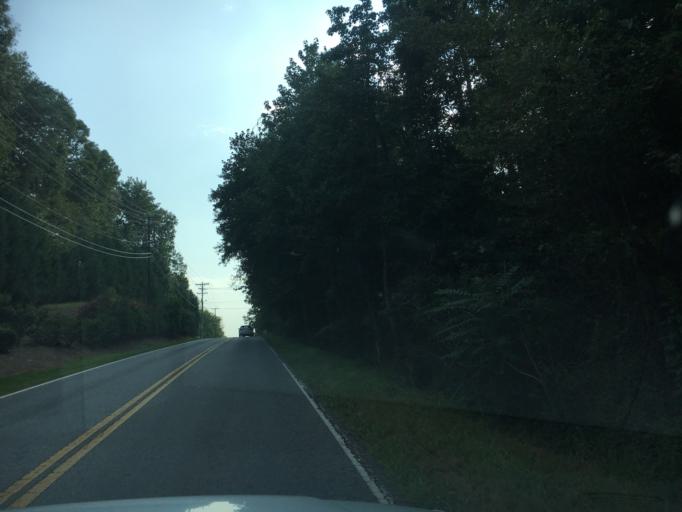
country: US
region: South Carolina
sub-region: Greenville County
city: Wade Hampton
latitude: 34.9346
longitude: -82.3392
